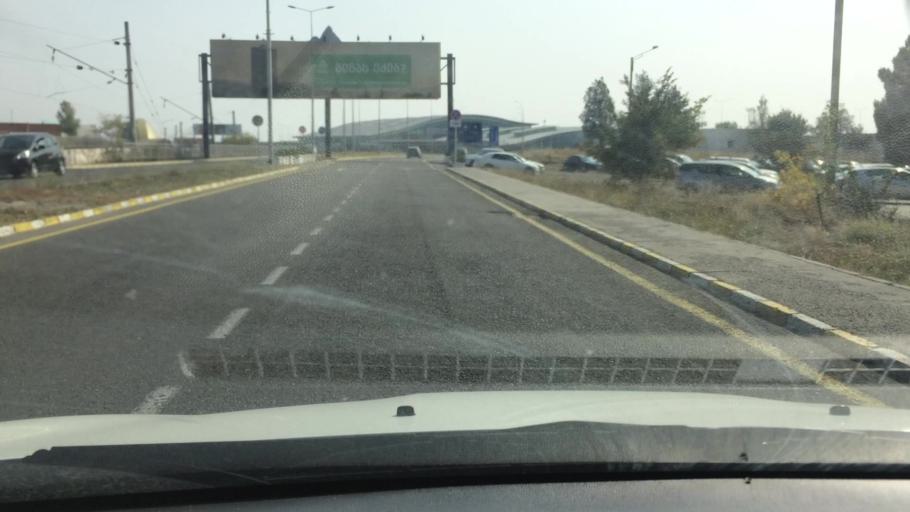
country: GE
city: Didi Lilo
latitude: 41.6735
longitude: 44.9622
